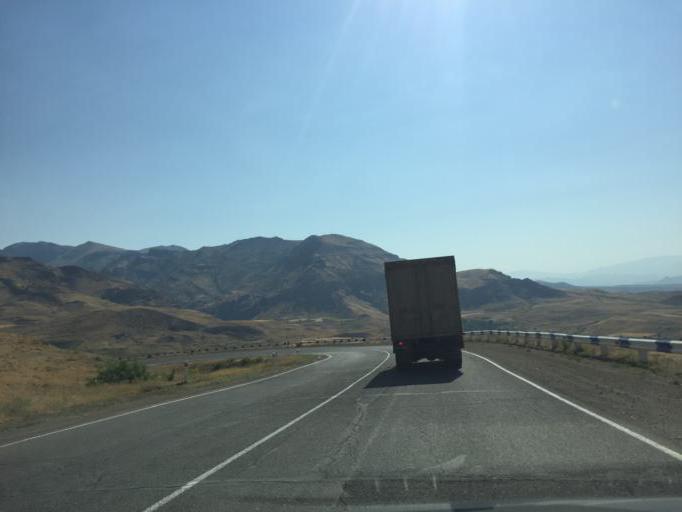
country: AM
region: Ararat
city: Zangakatun
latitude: 39.7966
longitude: 45.0998
